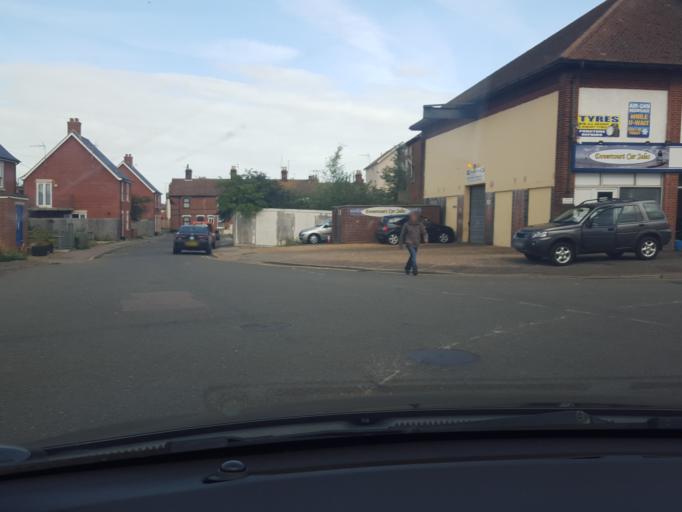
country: GB
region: England
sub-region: Essex
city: Dovercourt
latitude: 51.9385
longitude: 1.2807
